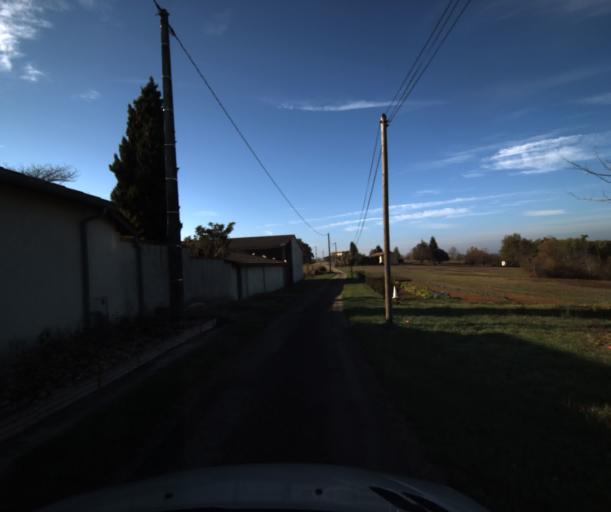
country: FR
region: Midi-Pyrenees
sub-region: Departement du Tarn-et-Garonne
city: Lafrancaise
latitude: 44.1088
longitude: 1.2892
